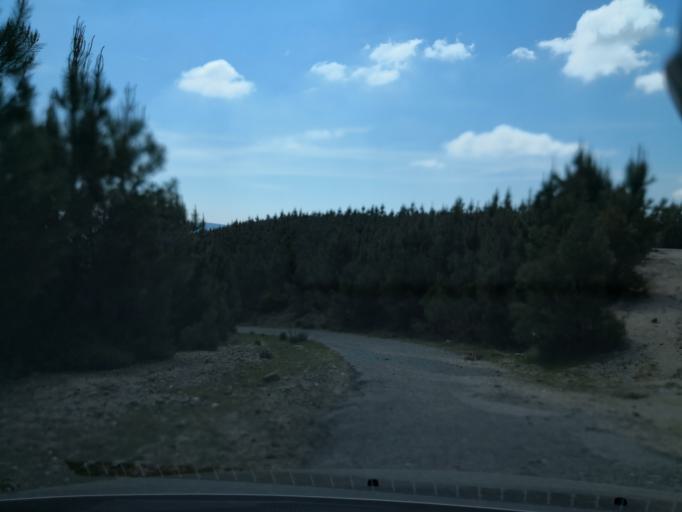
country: PT
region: Vila Real
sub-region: Vila Real
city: Vila Real
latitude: 41.3638
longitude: -7.7399
